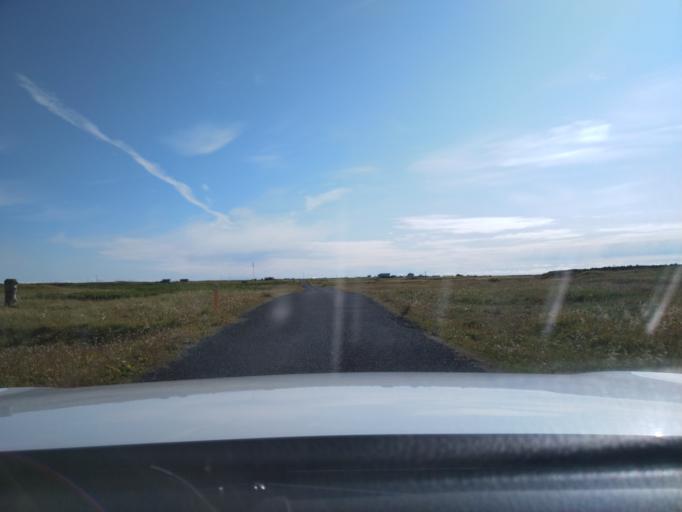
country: IS
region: South
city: THorlakshoefn
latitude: 63.8339
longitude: -21.6994
